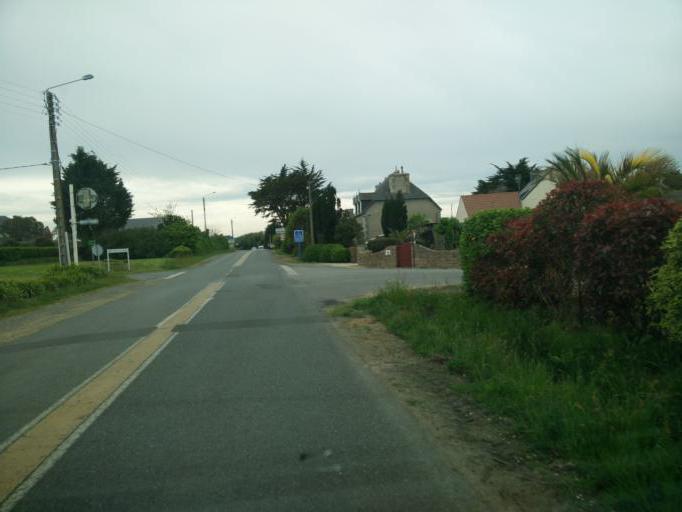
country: FR
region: Brittany
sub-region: Departement des Cotes-d'Armor
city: Tregastel
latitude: 48.8104
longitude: -3.5315
